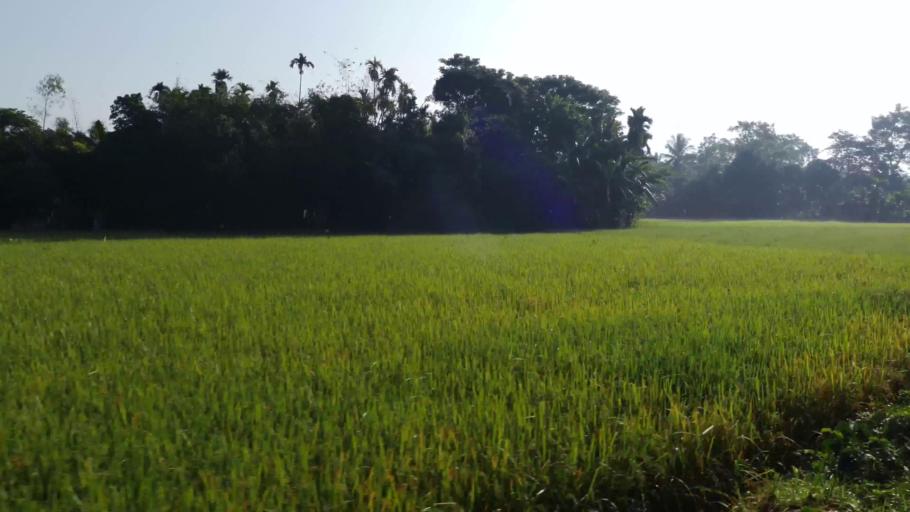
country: BD
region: Dhaka
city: Jamalpur
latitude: 24.8632
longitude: 90.0656
